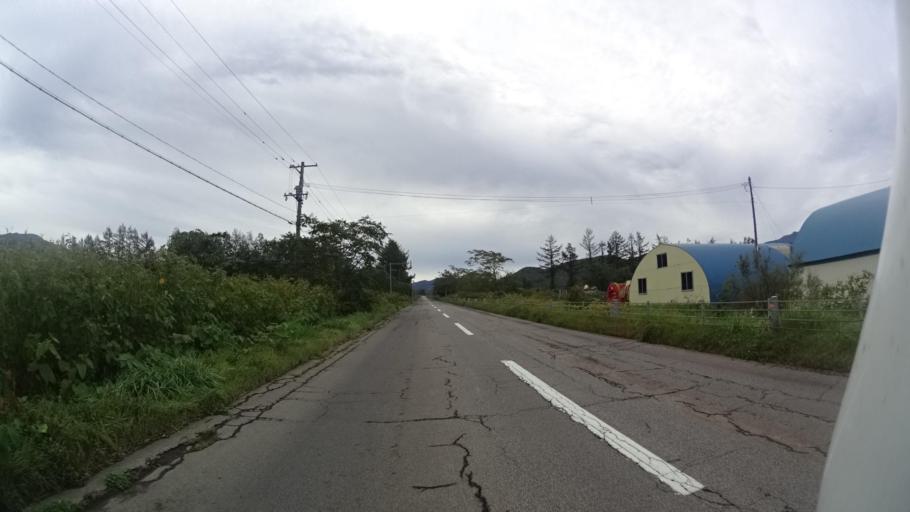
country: JP
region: Hokkaido
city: Shibetsu
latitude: 43.8601
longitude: 144.7613
